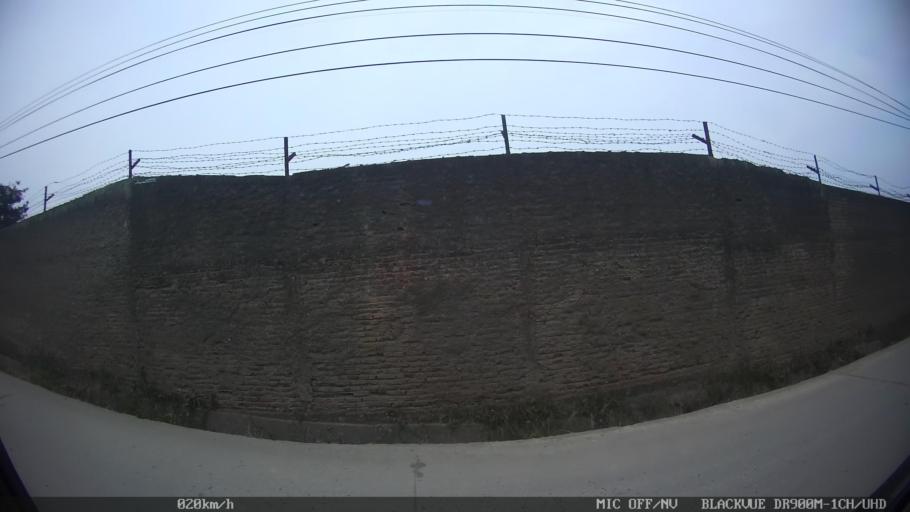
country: ID
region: Lampung
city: Panjang
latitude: -5.4361
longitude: 105.3264
